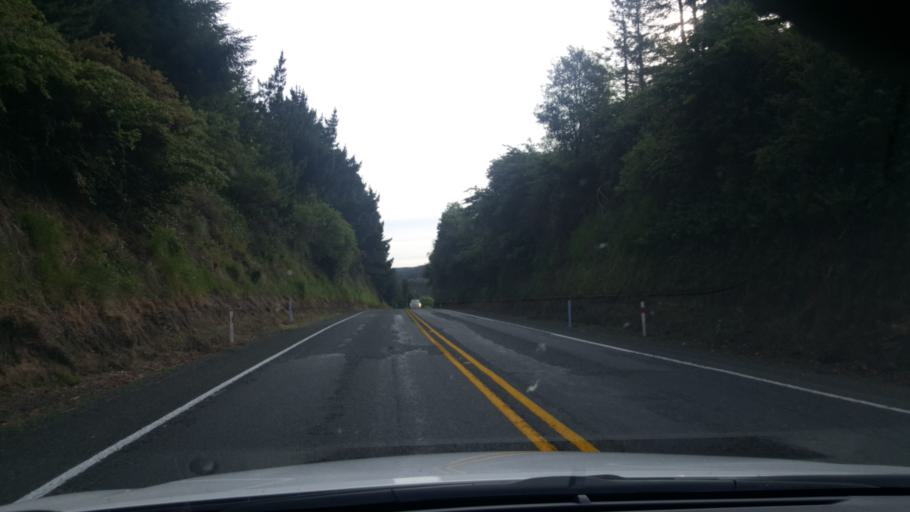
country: NZ
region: Waikato
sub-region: Taupo District
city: Taupo
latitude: -38.6213
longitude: 176.1053
